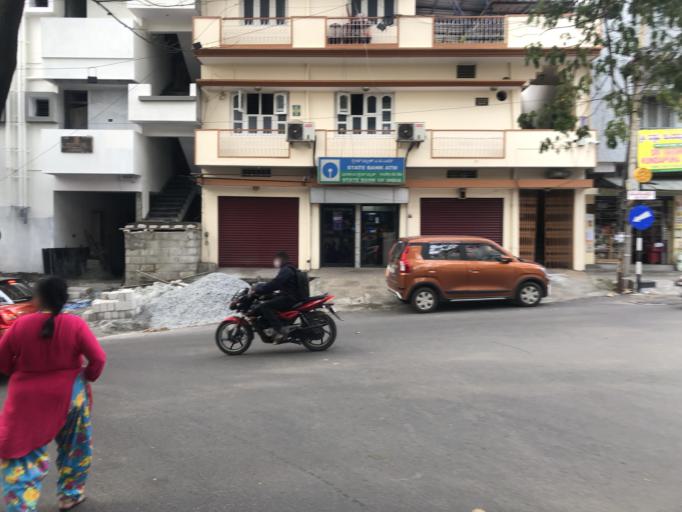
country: IN
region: Karnataka
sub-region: Bangalore Urban
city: Bangalore
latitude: 12.9405
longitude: 77.5478
